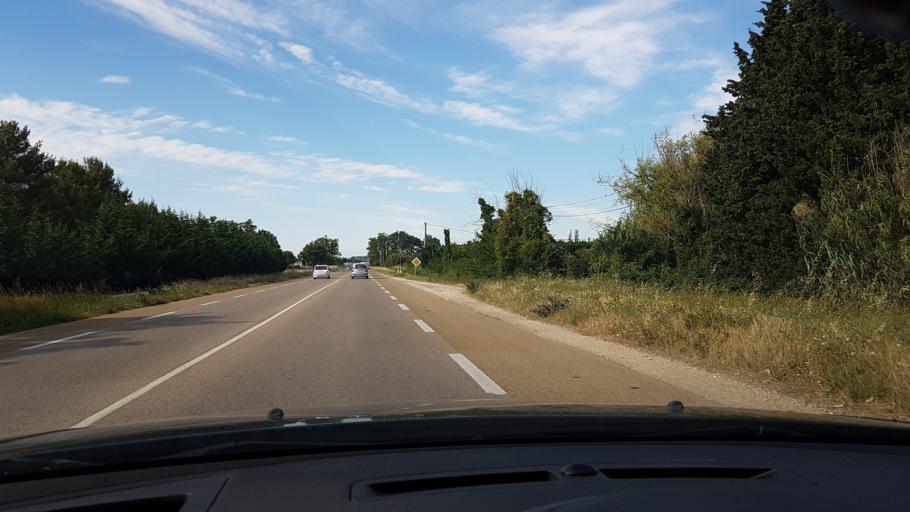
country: FR
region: Provence-Alpes-Cote d'Azur
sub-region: Departement des Bouches-du-Rhone
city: Graveson
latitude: 43.8742
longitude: 4.7729
